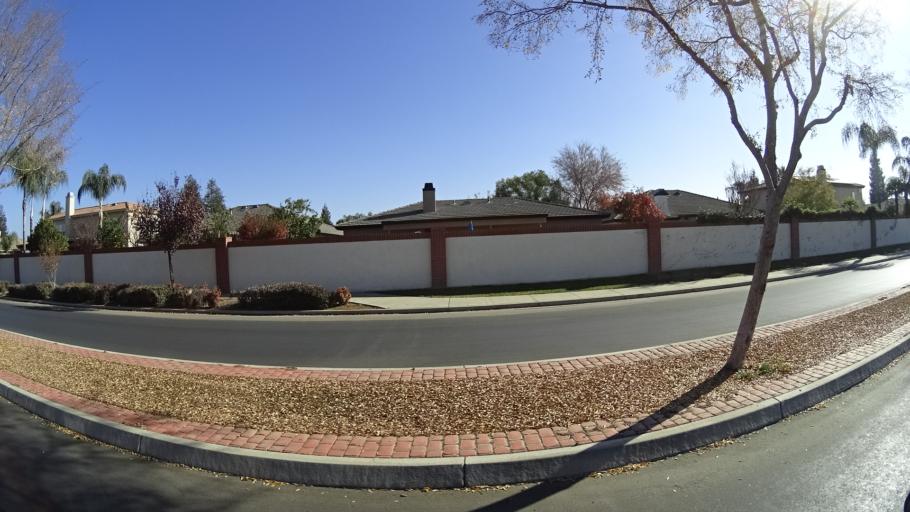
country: US
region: California
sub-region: Kern County
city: Rosedale
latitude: 35.3298
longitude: -119.1312
